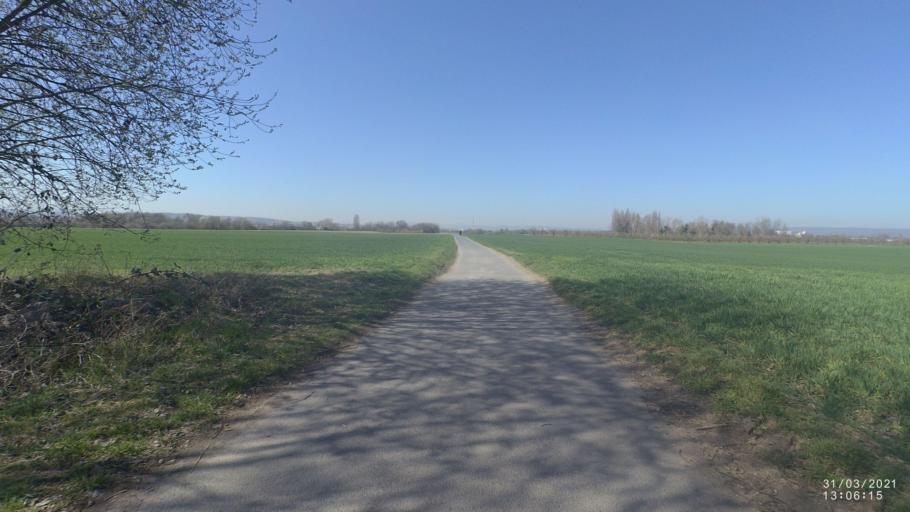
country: DE
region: Rheinland-Pfalz
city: Kaltenengers
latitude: 50.4039
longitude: 7.5389
